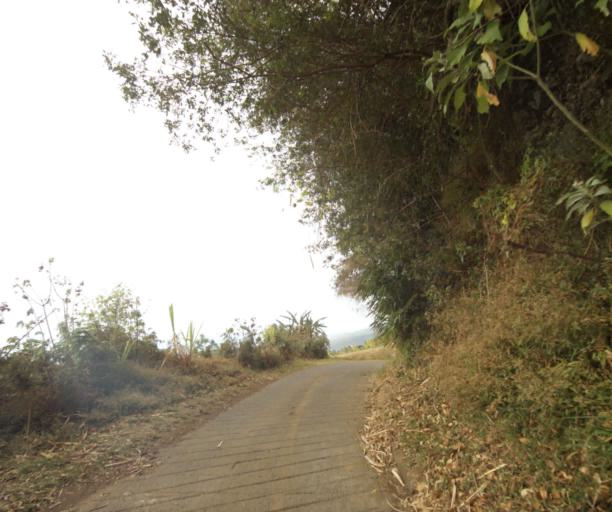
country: RE
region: Reunion
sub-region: Reunion
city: Saint-Paul
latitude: -21.0222
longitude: 55.3234
